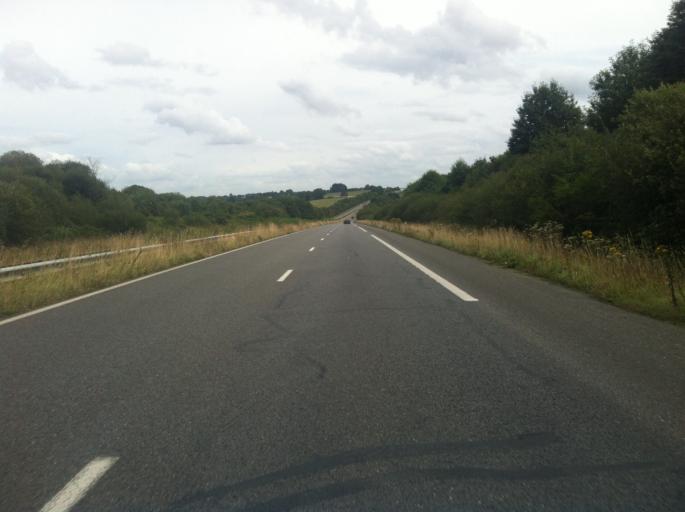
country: FR
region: Brittany
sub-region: Departement du Finistere
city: Plouneventer
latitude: 48.4909
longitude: -4.2234
